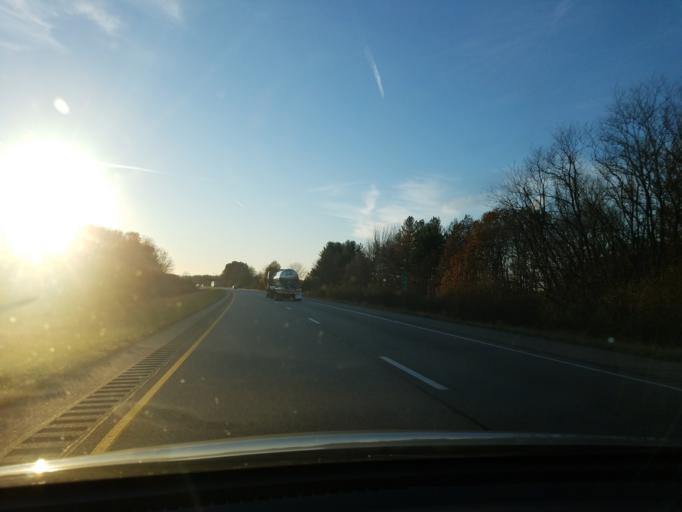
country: US
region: Indiana
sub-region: Warrick County
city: Chandler
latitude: 38.1841
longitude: -87.3894
